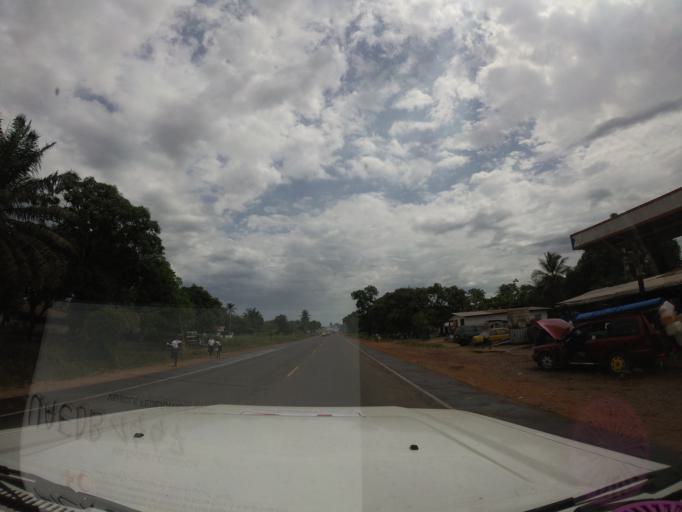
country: LR
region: Montserrado
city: Bensonville City
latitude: 6.3414
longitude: -10.6582
